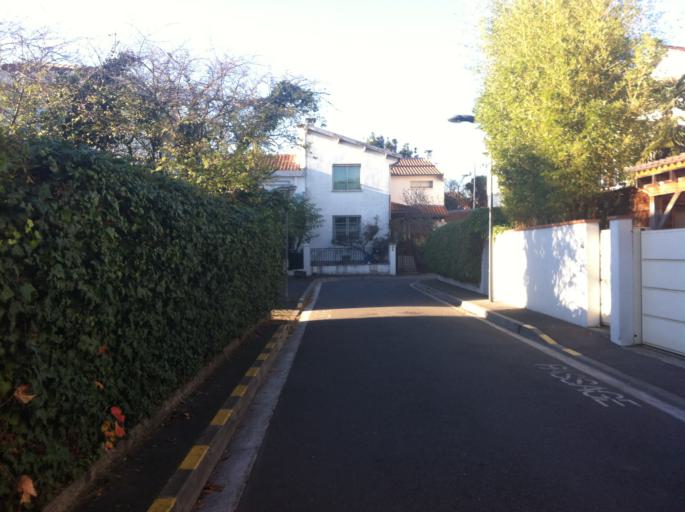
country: FR
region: Midi-Pyrenees
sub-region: Departement de la Haute-Garonne
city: Toulouse
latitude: 43.5889
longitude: 1.4678
